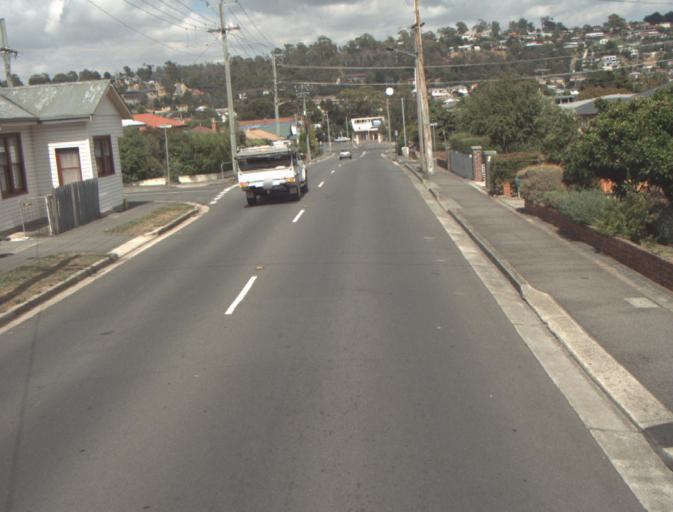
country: AU
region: Tasmania
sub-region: Launceston
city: East Launceston
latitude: -41.4682
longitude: 147.1632
